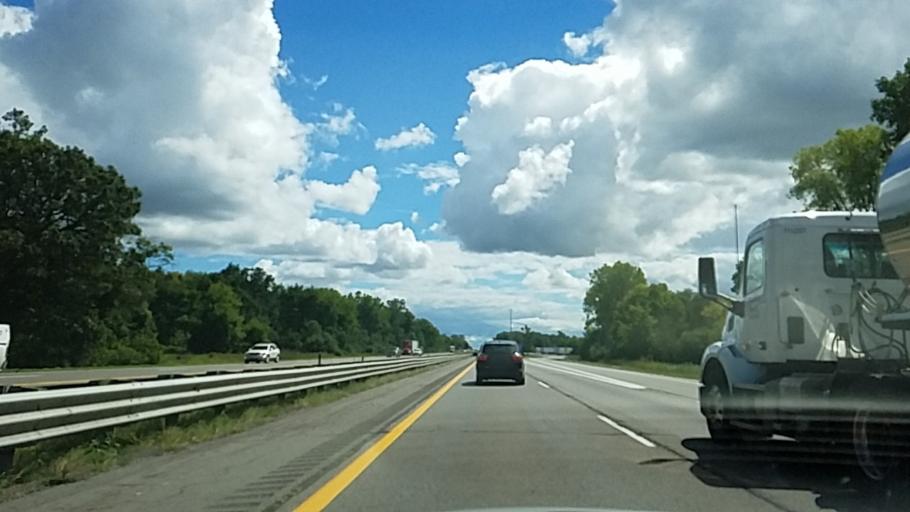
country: US
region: Michigan
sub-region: Livingston County
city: Whitmore Lake
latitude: 42.3594
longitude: -83.7488
